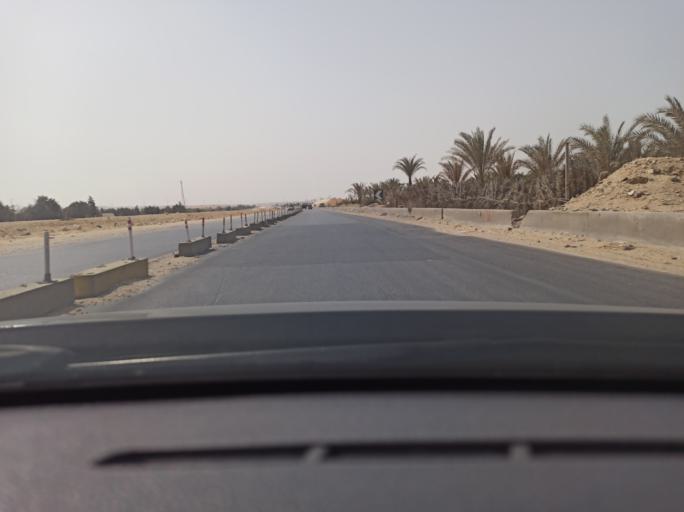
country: EG
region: Muhafazat al Fayyum
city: Al Wasitah
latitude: 29.2732
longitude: 31.2653
